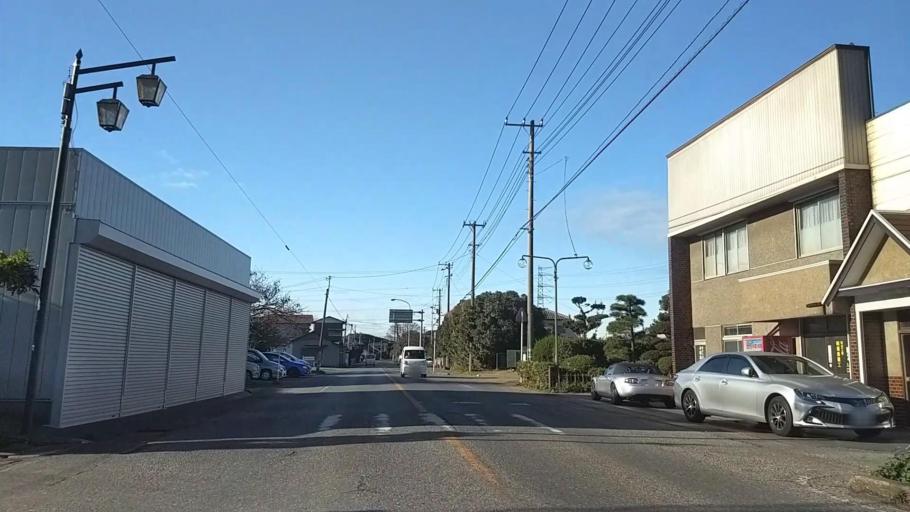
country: JP
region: Chiba
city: Futtsu
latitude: 35.3214
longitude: 139.8408
